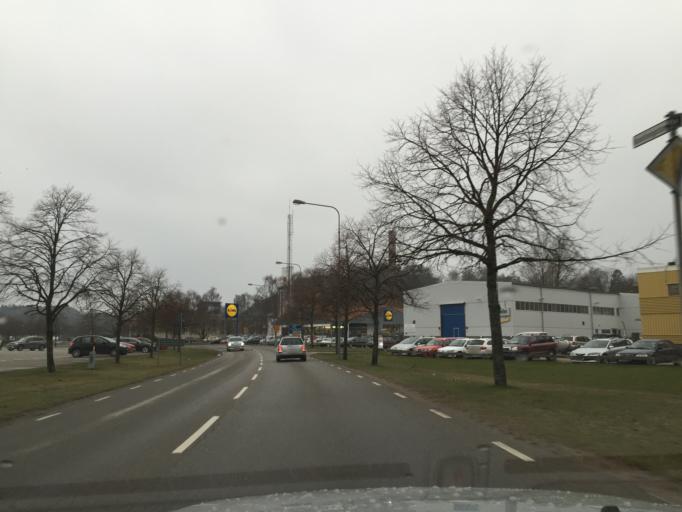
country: SE
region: Vaestra Goetaland
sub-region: Uddevalla Kommun
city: Uddevalla
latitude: 58.3512
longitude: 11.9287
